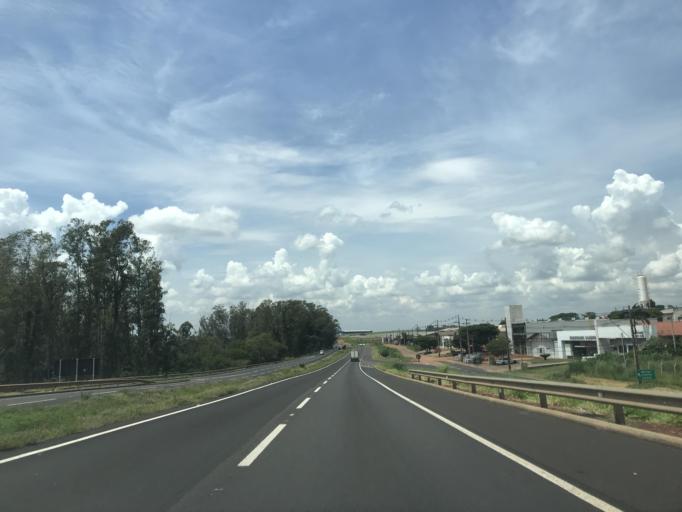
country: BR
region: Parana
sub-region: Alto Parana
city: Alto Parana
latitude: -23.2030
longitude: -52.1963
